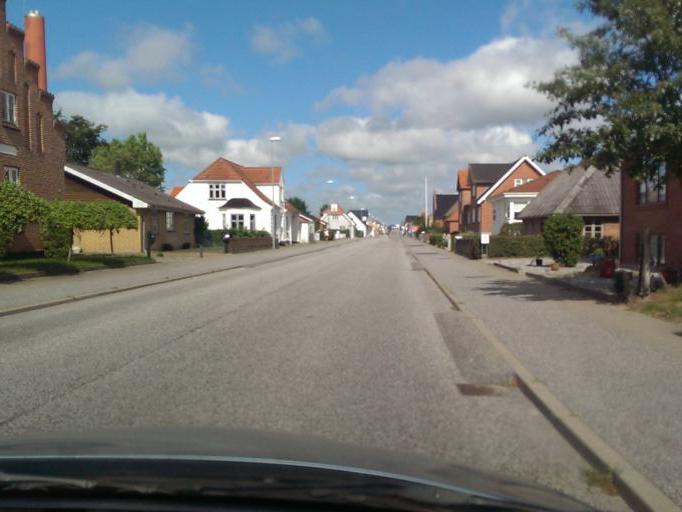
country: DK
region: North Denmark
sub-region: Alborg Kommune
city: Vestbjerg
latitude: 57.1944
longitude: 9.9504
